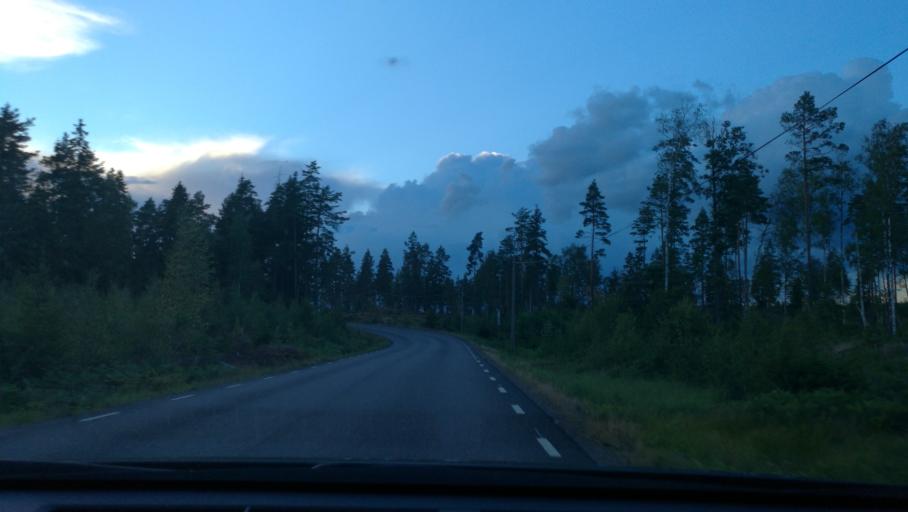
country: SE
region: OEstergoetland
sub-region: Norrkopings Kommun
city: Jursla
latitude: 58.8020
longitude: 16.1340
